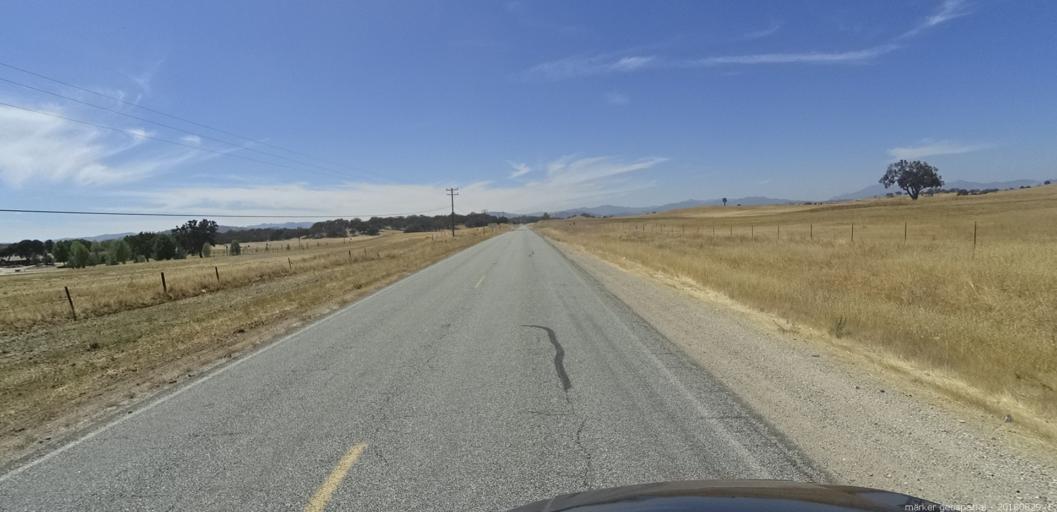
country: US
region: California
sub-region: Monterey County
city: King City
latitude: 35.9369
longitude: -121.0889
